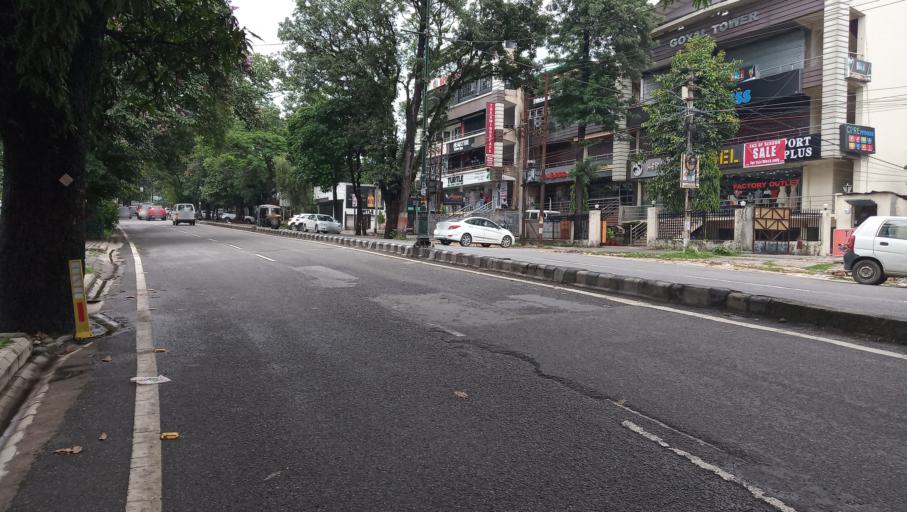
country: IN
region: Uttarakhand
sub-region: Dehradun
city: Dehradun
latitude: 30.3687
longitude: 78.0741
